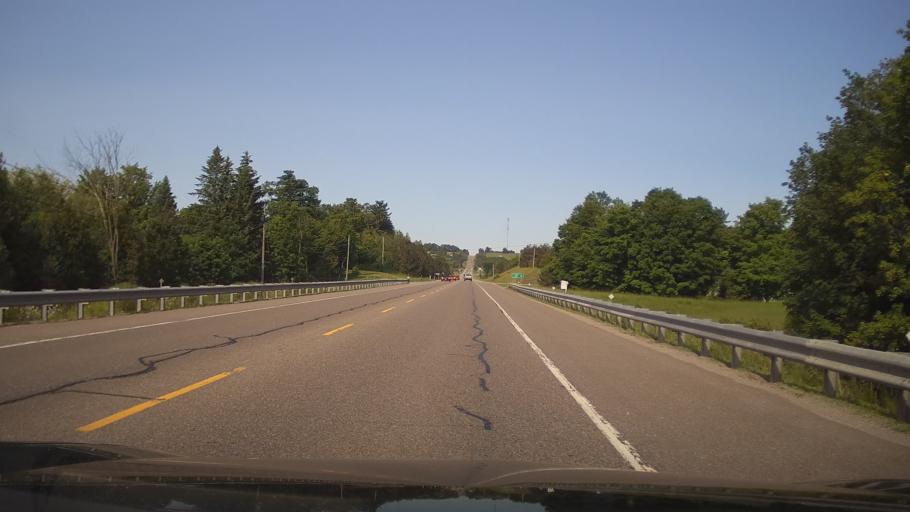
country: CA
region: Ontario
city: Omemee
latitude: 44.3225
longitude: -78.4638
